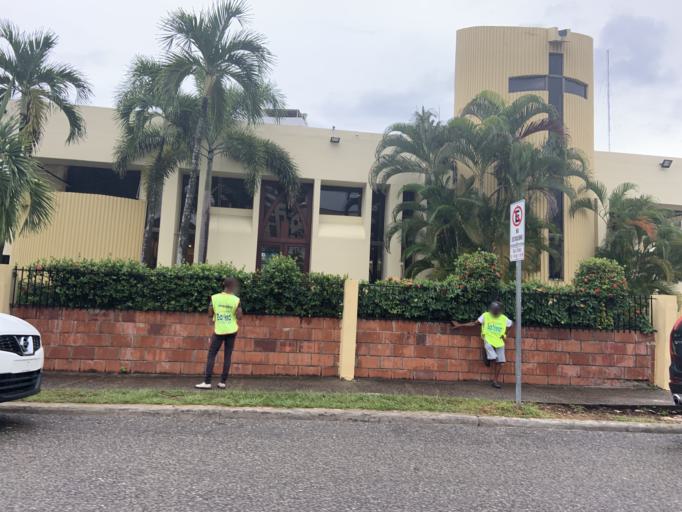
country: DO
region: Nacional
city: La Julia
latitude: 18.4770
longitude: -69.9249
